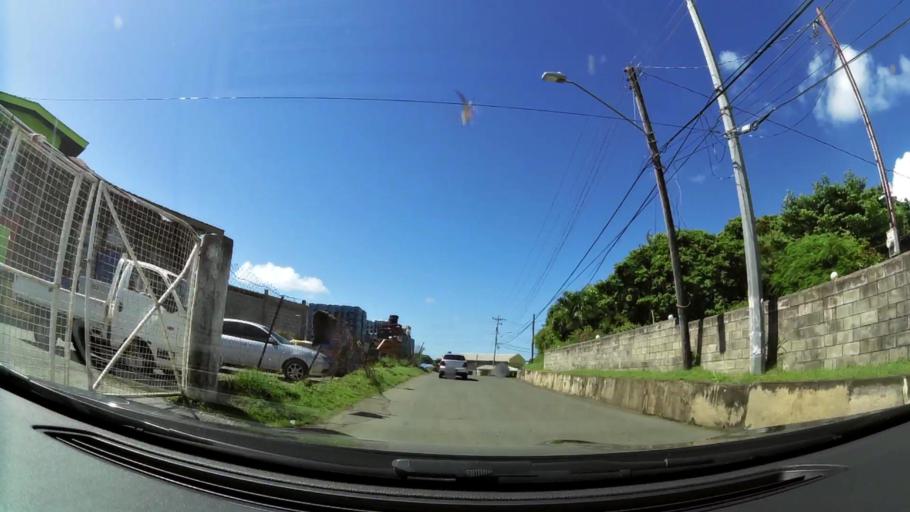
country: TT
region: Tobago
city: Scarborough
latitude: 11.1689
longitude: -60.7875
